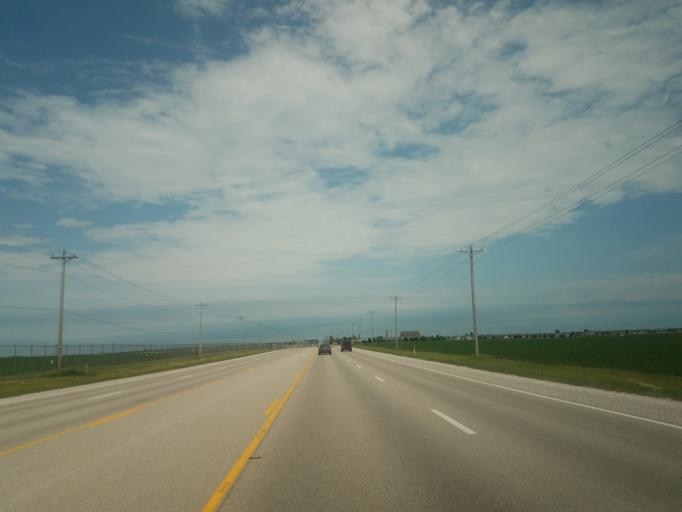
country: US
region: Illinois
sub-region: McLean County
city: Downs
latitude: 40.4805
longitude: -88.9024
